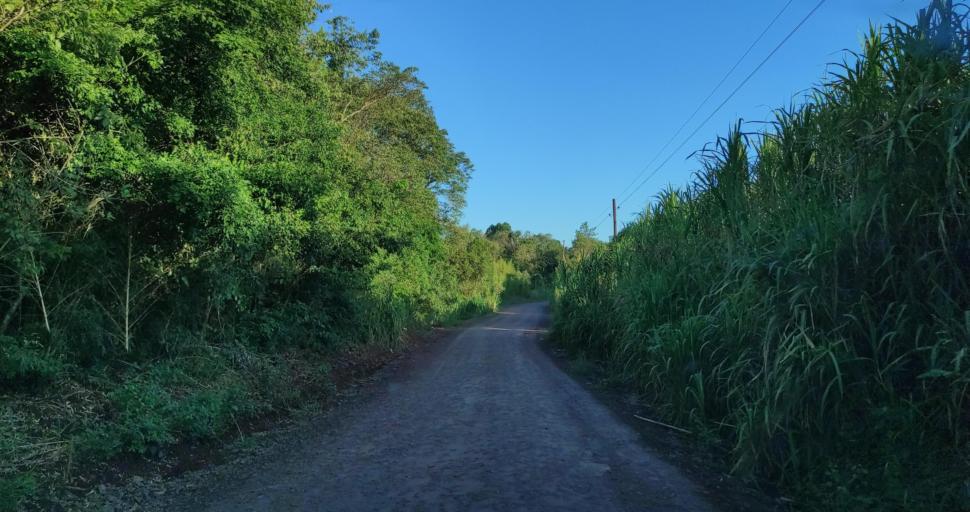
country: AR
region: Misiones
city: Gobernador Roca
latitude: -27.2044
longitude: -55.4567
